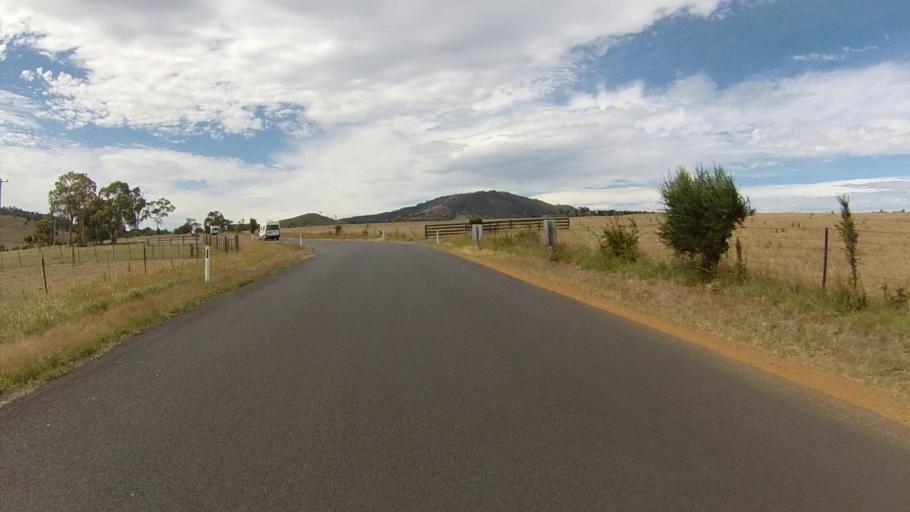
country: AU
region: Tasmania
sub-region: Brighton
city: Old Beach
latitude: -42.7149
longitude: 147.3224
